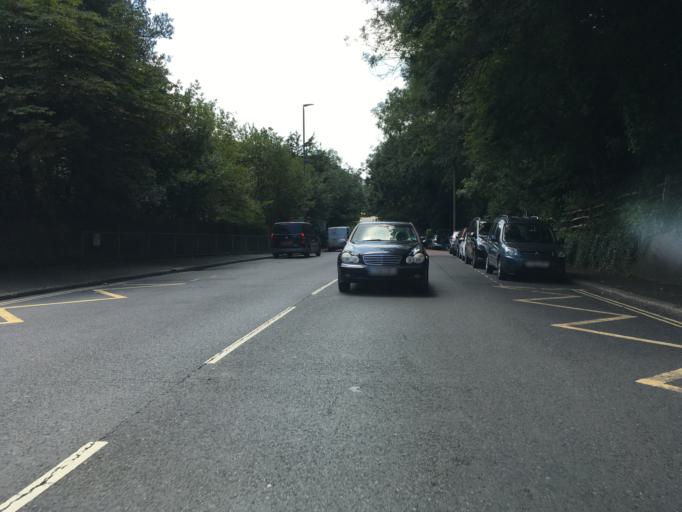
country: GB
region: England
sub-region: East Sussex
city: Hastings
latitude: 50.8632
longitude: 0.5974
